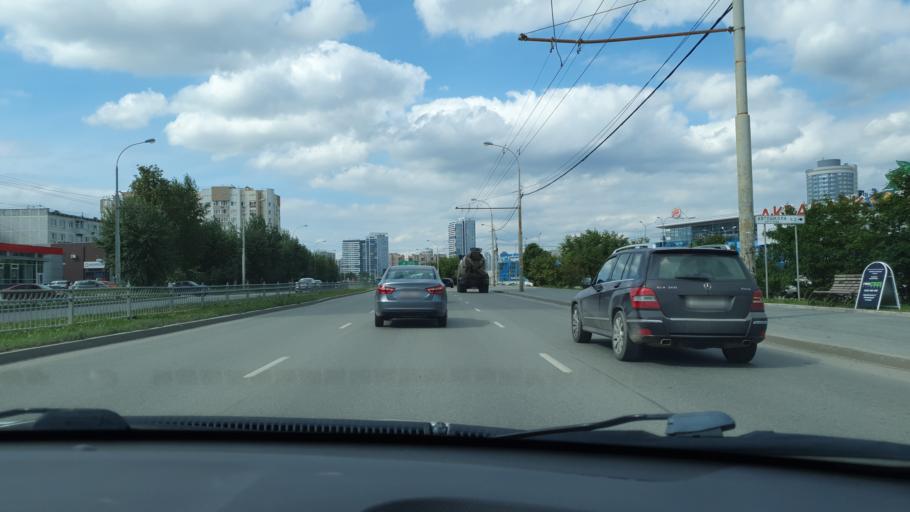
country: RU
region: Sverdlovsk
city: Yekaterinburg
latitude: 56.7891
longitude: 60.6464
